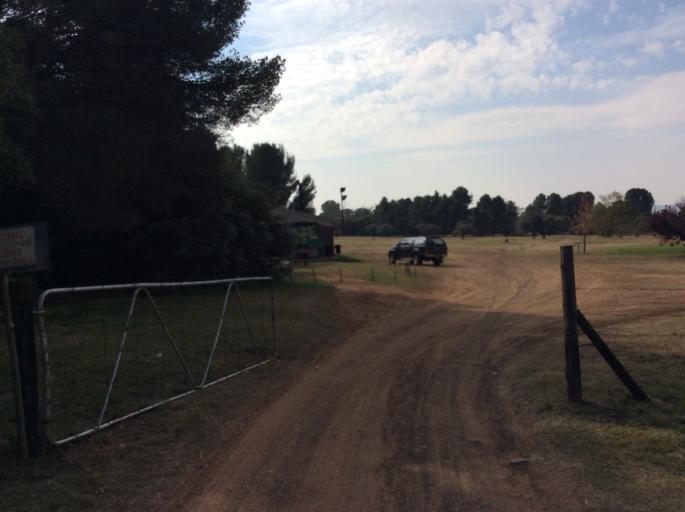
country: ZA
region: Orange Free State
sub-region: Xhariep District Municipality
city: Dewetsdorp
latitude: -29.5758
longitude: 26.6645
